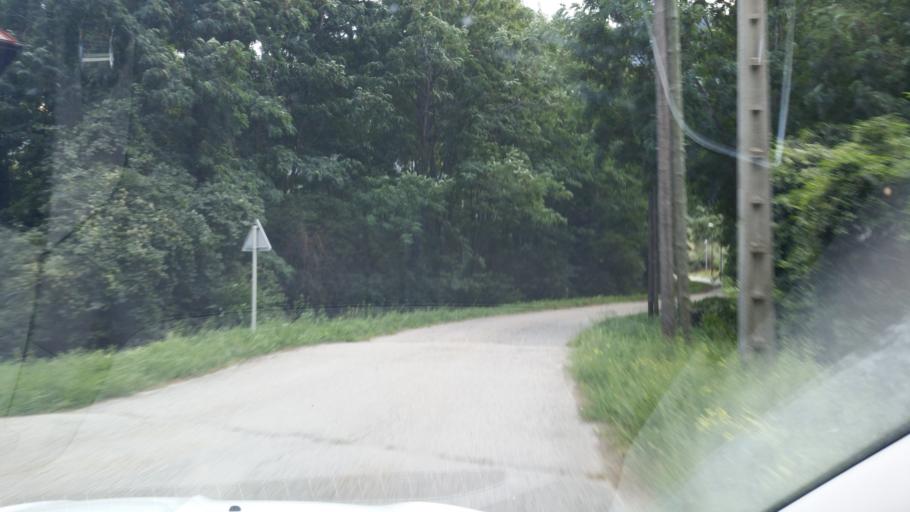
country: FR
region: Rhone-Alpes
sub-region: Departement de la Savoie
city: Villargondran
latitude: 45.2767
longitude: 6.3696
